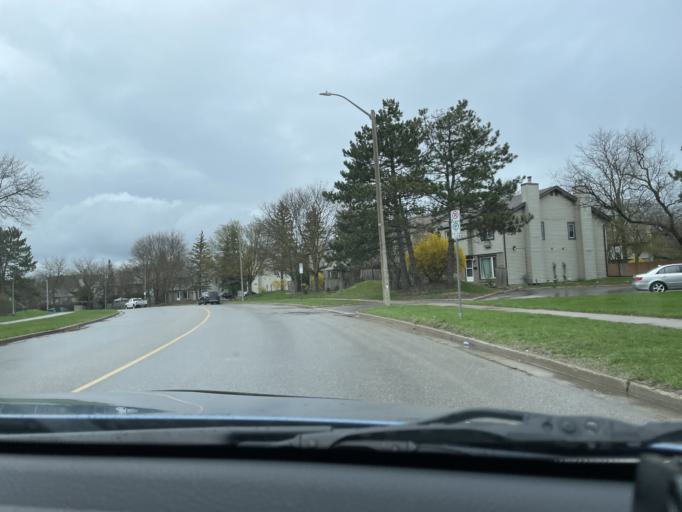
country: CA
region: Ontario
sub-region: Wellington County
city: Guelph
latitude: 43.5194
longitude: -80.2390
